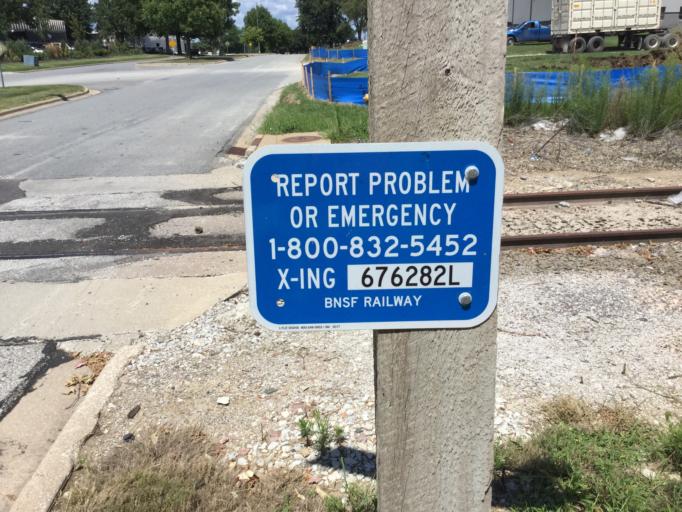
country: US
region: Kansas
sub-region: Johnson County
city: Lenexa
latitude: 38.9503
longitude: -94.7574
